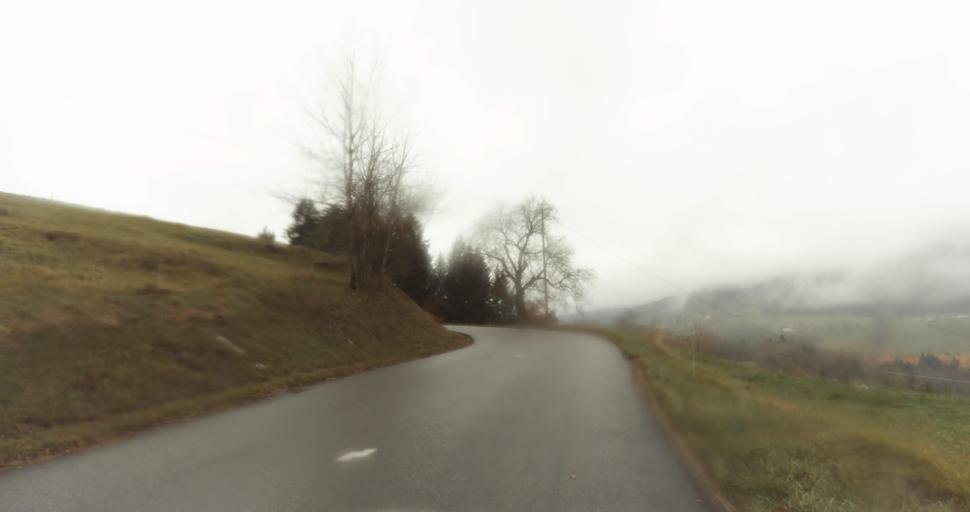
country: FR
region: Rhone-Alpes
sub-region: Departement de la Haute-Savoie
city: Thorens-Glieres
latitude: 46.0008
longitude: 6.2496
